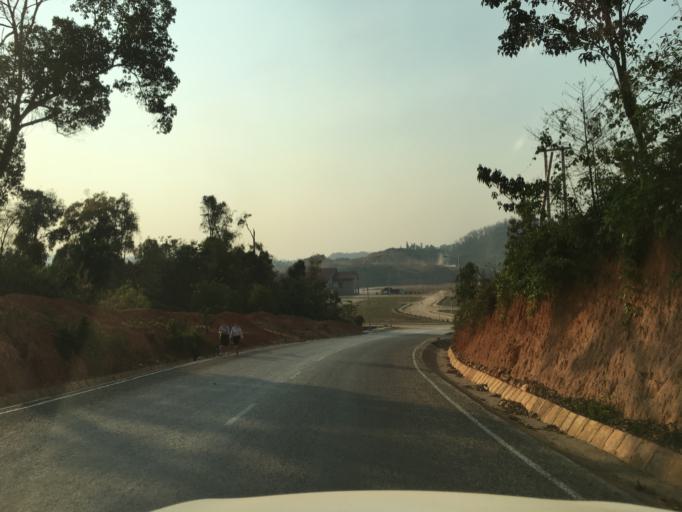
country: LA
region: Houaphan
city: Xam Nua
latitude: 20.6095
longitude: 104.0729
